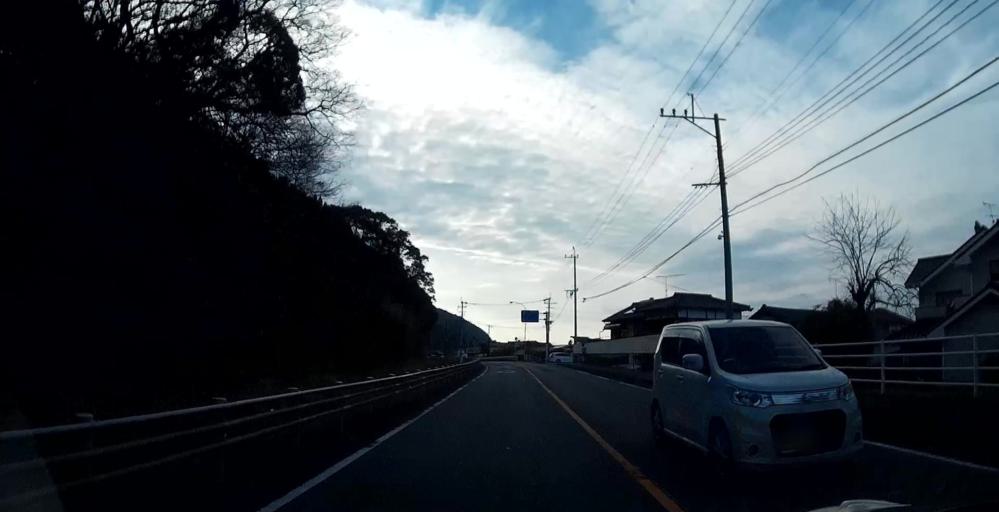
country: JP
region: Kumamoto
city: Matsubase
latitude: 32.6662
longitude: 130.5420
